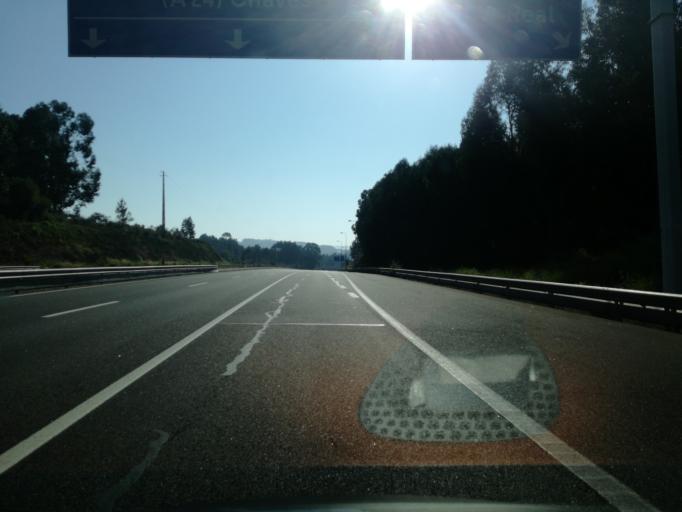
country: PT
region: Porto
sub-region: Maia
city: Nogueira
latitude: 41.2398
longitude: -8.5725
